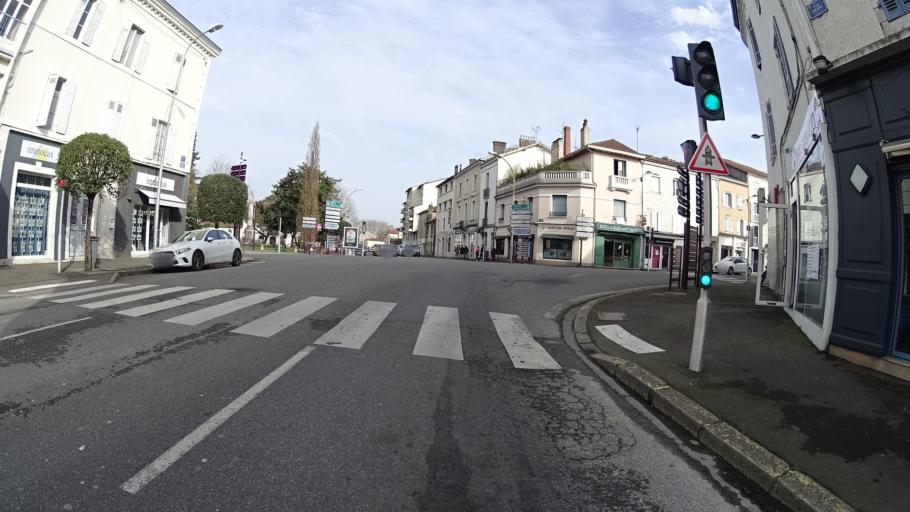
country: FR
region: Aquitaine
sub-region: Departement des Landes
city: Dax
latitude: 43.7074
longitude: -1.0530
